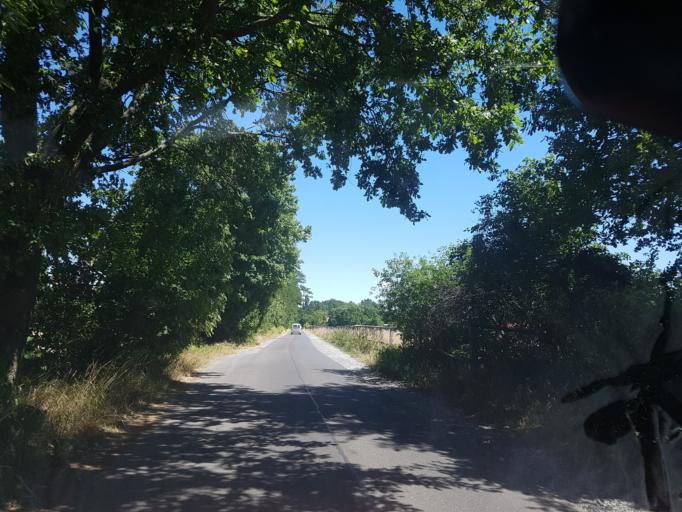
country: DE
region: Brandenburg
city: Teltow
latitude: 52.3846
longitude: 13.2541
